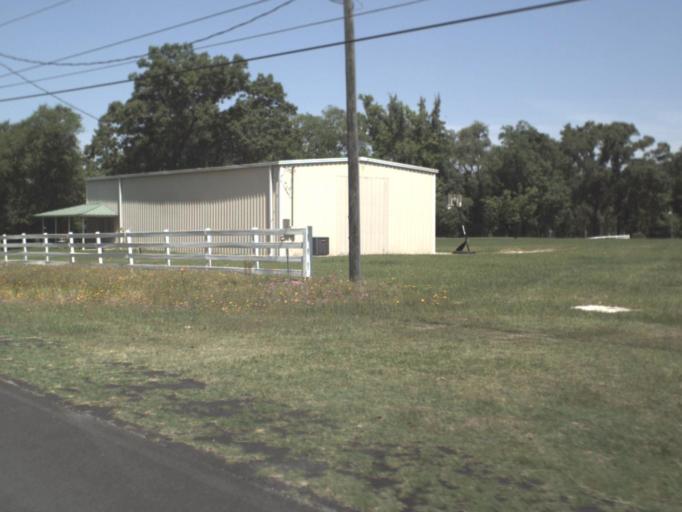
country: US
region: Florida
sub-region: Suwannee County
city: Wellborn
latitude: 30.2019
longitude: -82.7813
